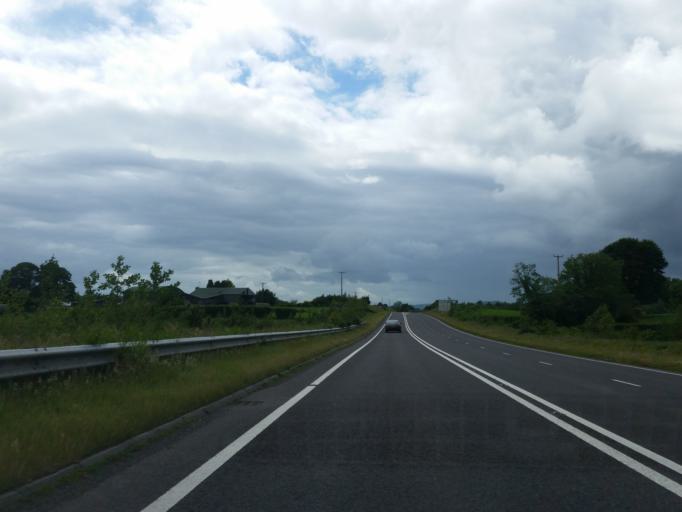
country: GB
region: Northern Ireland
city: Fivemiletown
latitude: 54.4413
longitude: -7.0875
